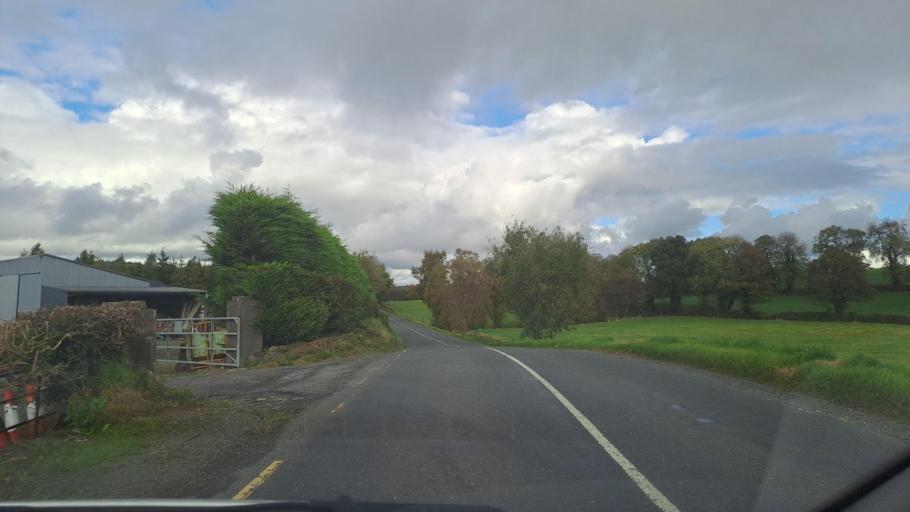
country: IE
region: Ulster
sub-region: An Cabhan
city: Mullagh
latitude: 53.8186
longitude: -6.9490
